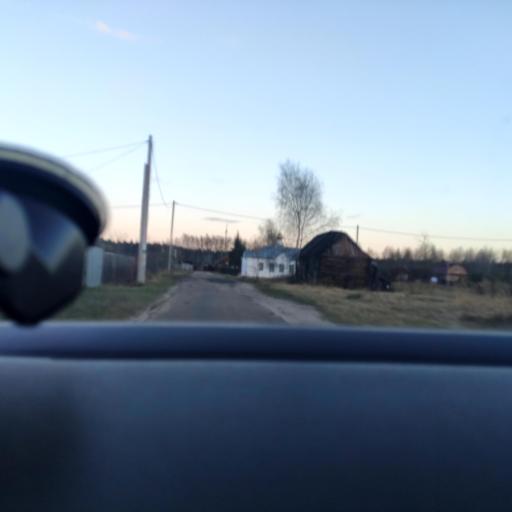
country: RU
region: Moskovskaya
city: Shaturtorf
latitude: 55.4349
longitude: 39.4272
